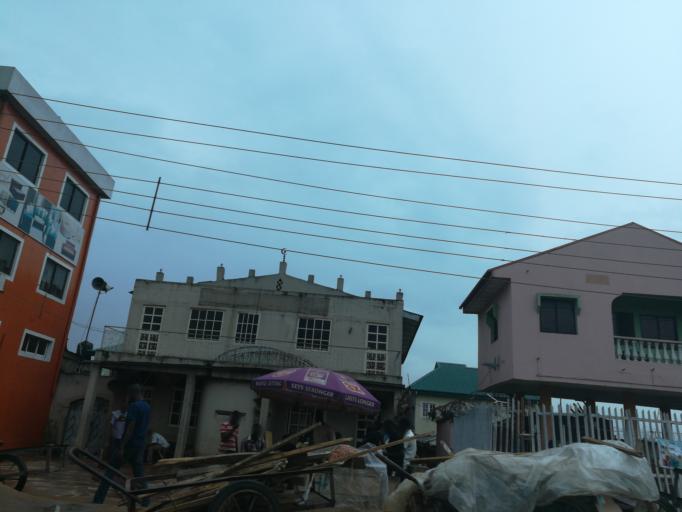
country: NG
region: Lagos
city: Oshodi
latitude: 6.5767
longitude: 3.3431
